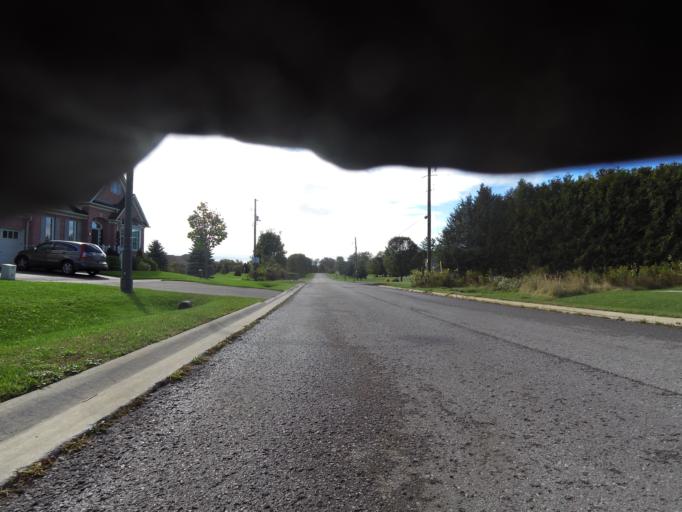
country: CA
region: Ontario
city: Cobourg
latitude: 43.9454
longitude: -78.3215
